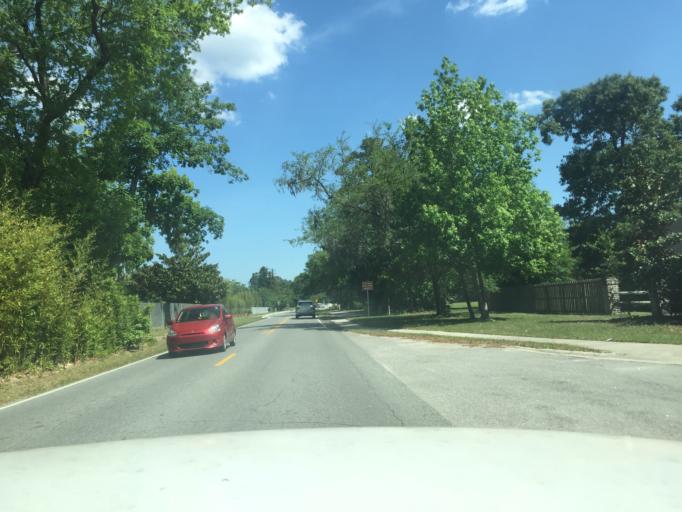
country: US
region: Georgia
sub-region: Chatham County
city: Georgetown
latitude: 31.9979
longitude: -81.2725
